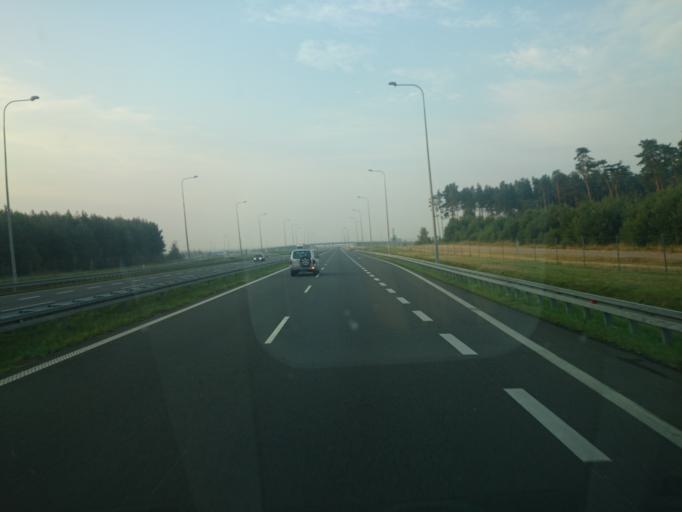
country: PL
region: West Pomeranian Voivodeship
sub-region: Powiat pyrzycki
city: Bielice
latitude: 53.1555
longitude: 14.7103
